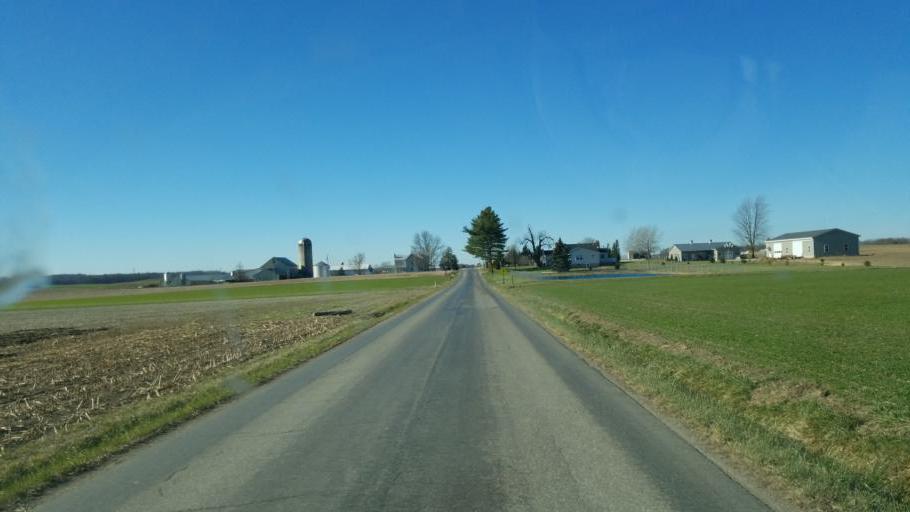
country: US
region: Ohio
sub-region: Huron County
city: Greenwich
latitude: 40.9608
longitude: -82.5353
